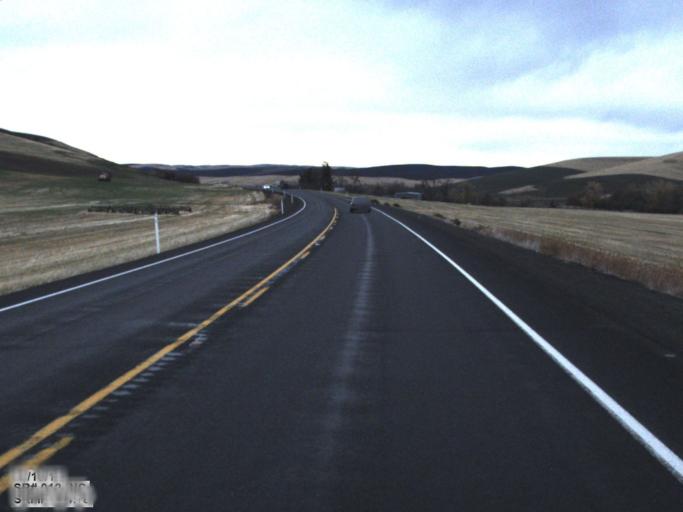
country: US
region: Washington
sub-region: Walla Walla County
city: Waitsburg
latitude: 46.2316
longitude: -118.1379
